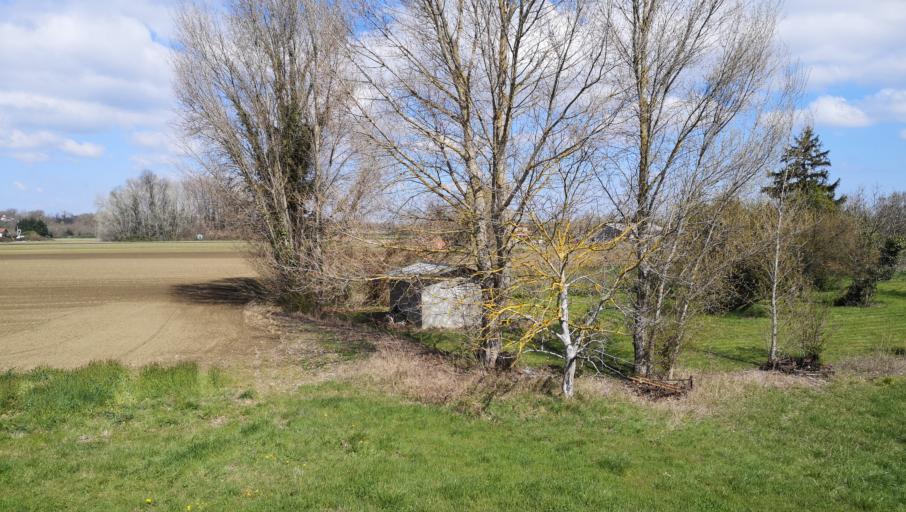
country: FR
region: Midi-Pyrenees
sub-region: Departement de la Haute-Garonne
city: Blagnac
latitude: 43.6450
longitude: 1.3957
